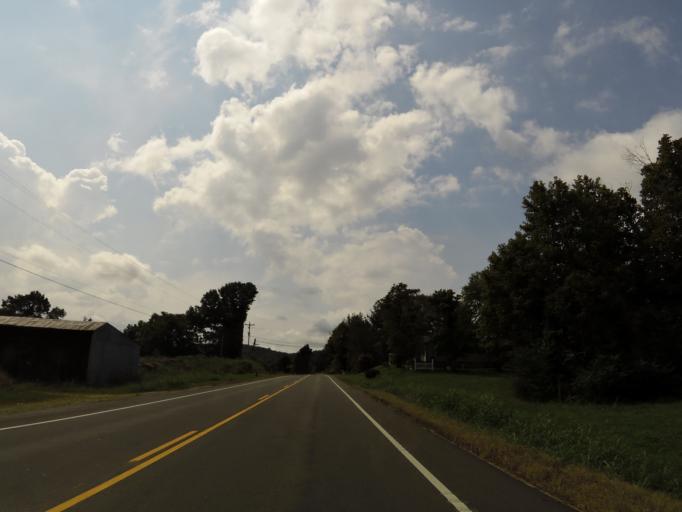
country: US
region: Tennessee
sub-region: Perry County
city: Linden
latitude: 35.7403
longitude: -87.8104
